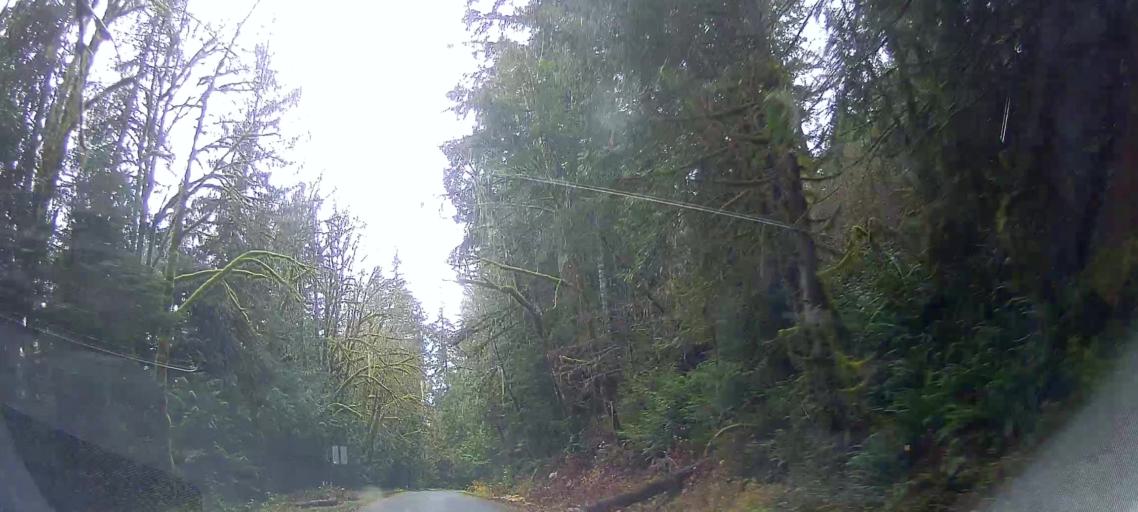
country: US
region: Washington
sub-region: Snohomish County
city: Darrington
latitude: 48.5210
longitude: -121.3713
